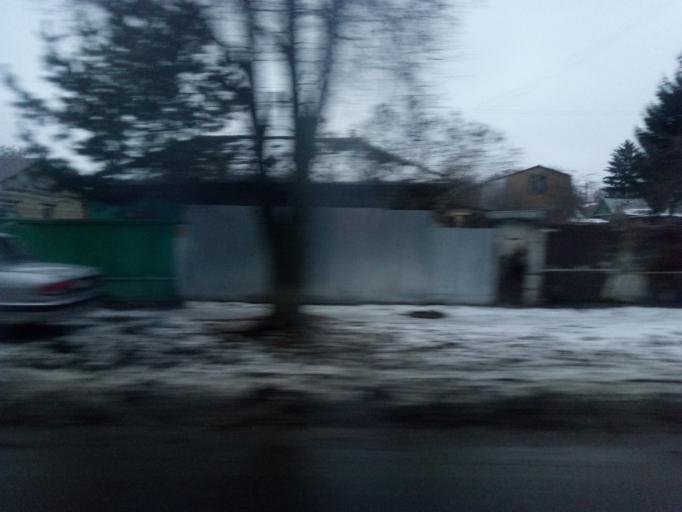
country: RU
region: Tula
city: Tula
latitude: 54.2021
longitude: 37.5565
